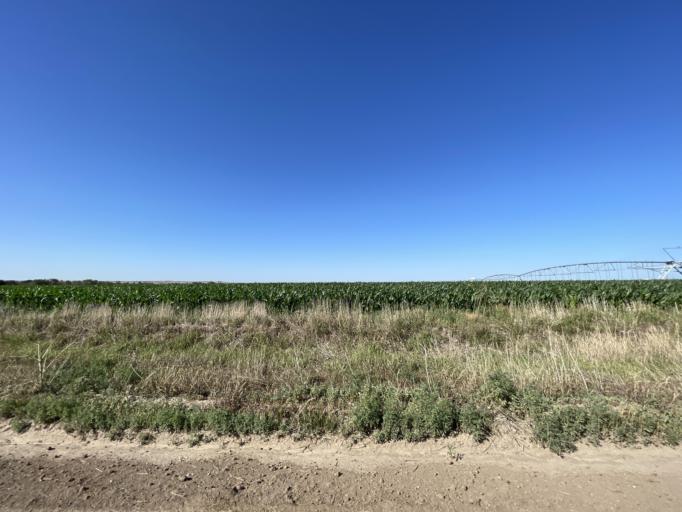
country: US
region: Nebraska
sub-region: Red Willow County
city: McCook
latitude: 40.2130
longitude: -100.6032
